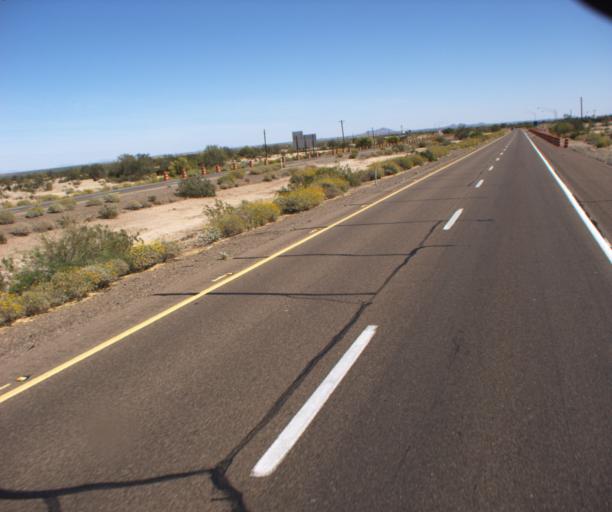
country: US
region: Arizona
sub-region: Yuma County
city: Wellton
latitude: 32.7300
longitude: -113.7232
